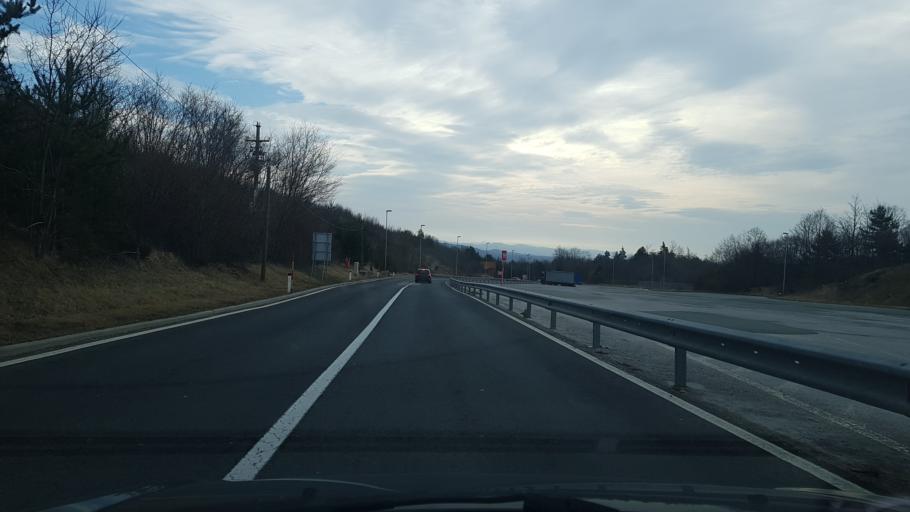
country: SI
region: Ilirska Bistrica
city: Ilirska Bistrica
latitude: 45.4933
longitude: 14.1997
